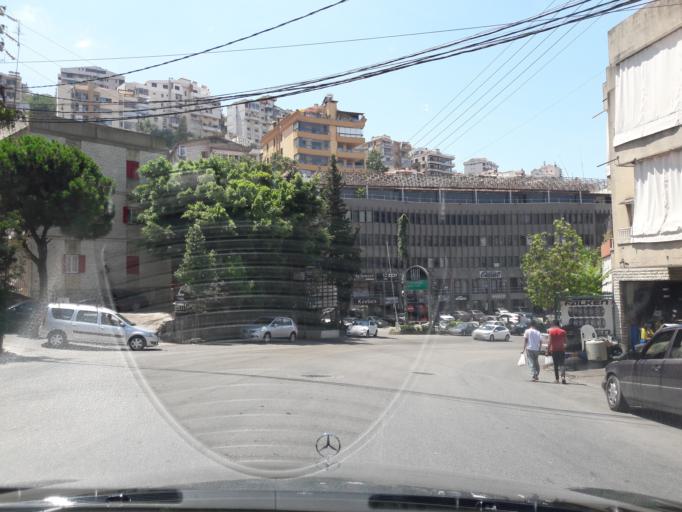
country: LB
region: Mont-Liban
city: Djounie
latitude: 33.9253
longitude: 35.6338
